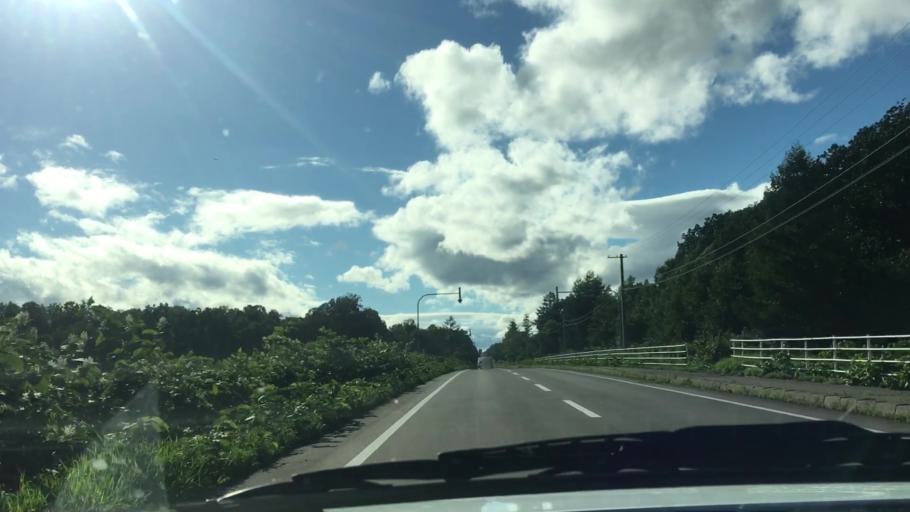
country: JP
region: Hokkaido
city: Otofuke
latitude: 43.1682
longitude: 143.1226
